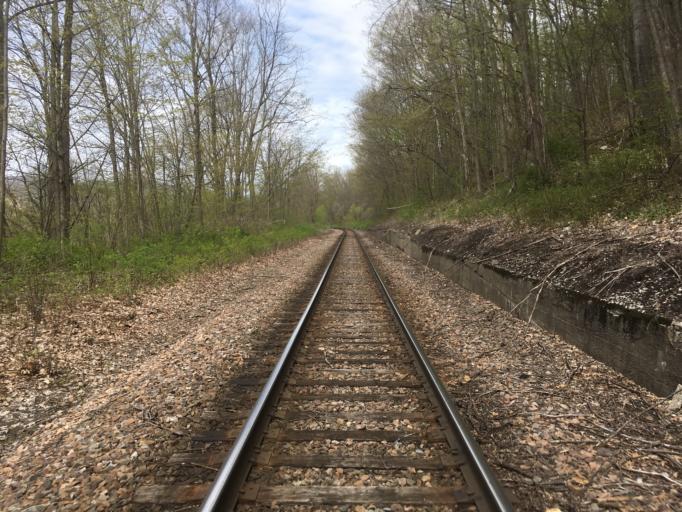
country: US
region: Vermont
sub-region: Rutland County
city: Brandon
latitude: 43.7125
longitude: -73.0401
